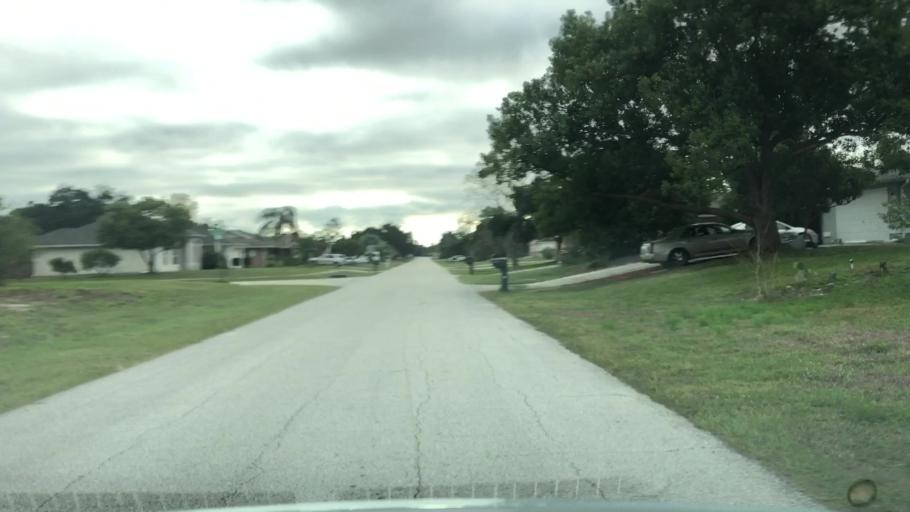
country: US
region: Florida
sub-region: Volusia County
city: Deltona
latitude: 28.8800
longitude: -81.2403
